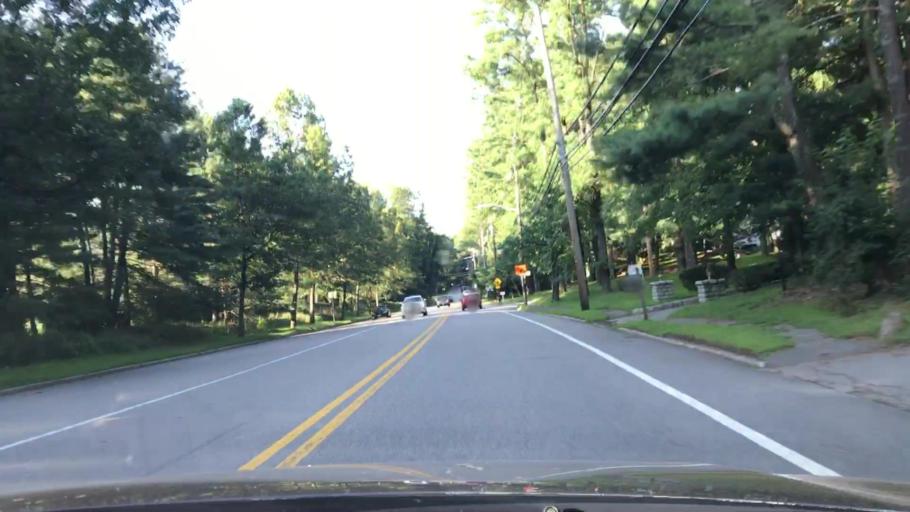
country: US
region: New Jersey
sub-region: Bergen County
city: Northvale
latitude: 40.9863
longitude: -73.9368
